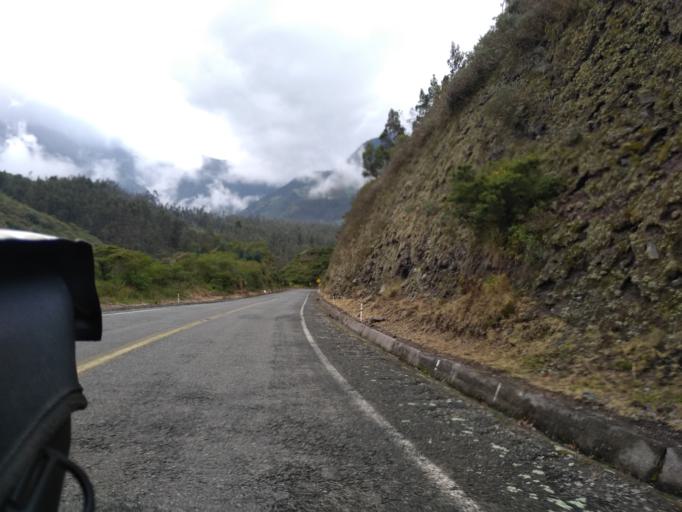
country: EC
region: Chimborazo
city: Guano
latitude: -1.5215
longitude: -78.5121
